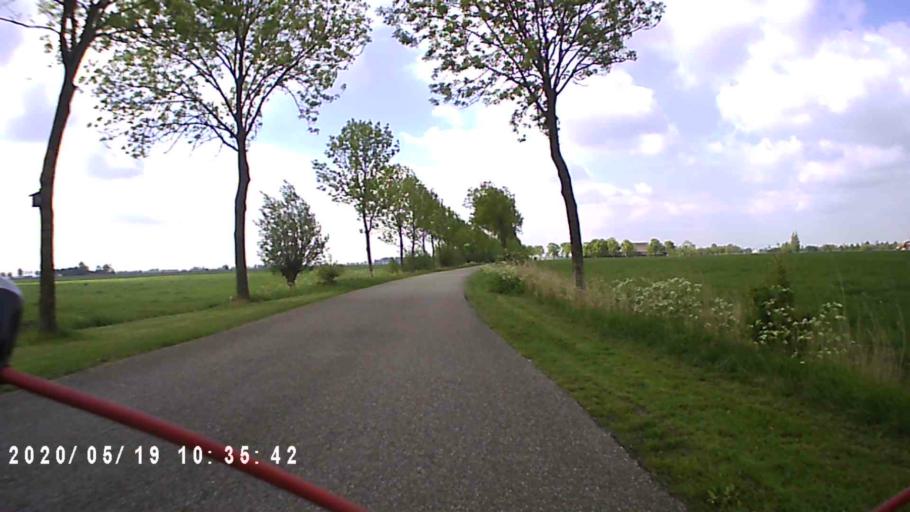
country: NL
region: Friesland
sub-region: Gemeente Kollumerland en Nieuwkruisland
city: Kollum
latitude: 53.2801
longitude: 6.1846
